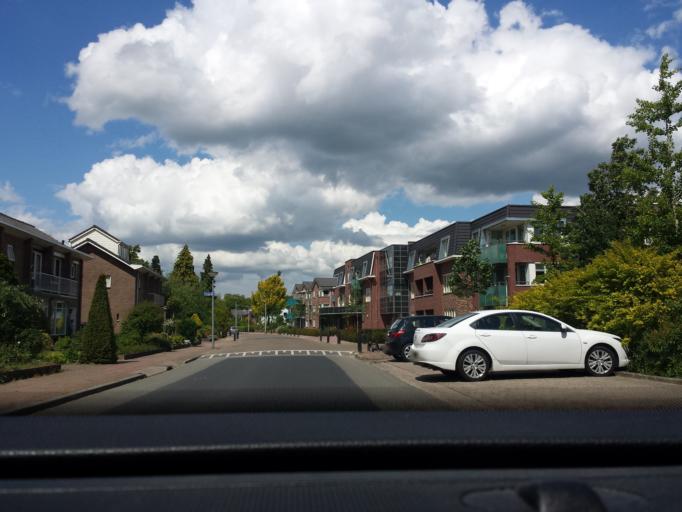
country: NL
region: Gelderland
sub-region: Gemeente Zutphen
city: Warnsveld
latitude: 52.1382
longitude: 6.2300
